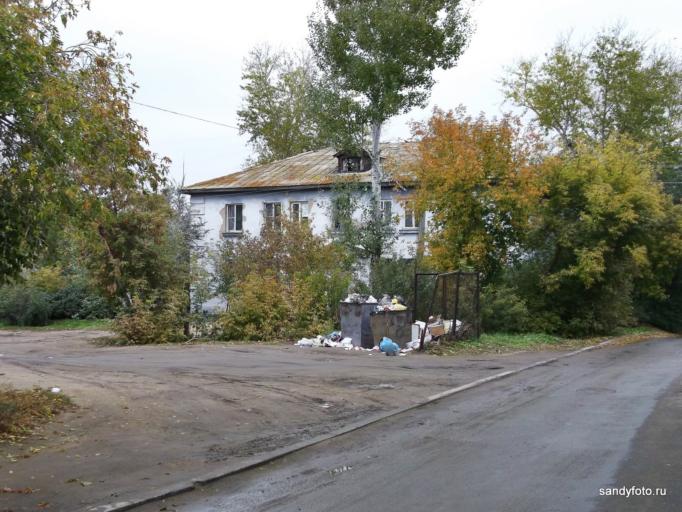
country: RU
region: Chelyabinsk
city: Troitsk
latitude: 54.0855
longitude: 61.5439
